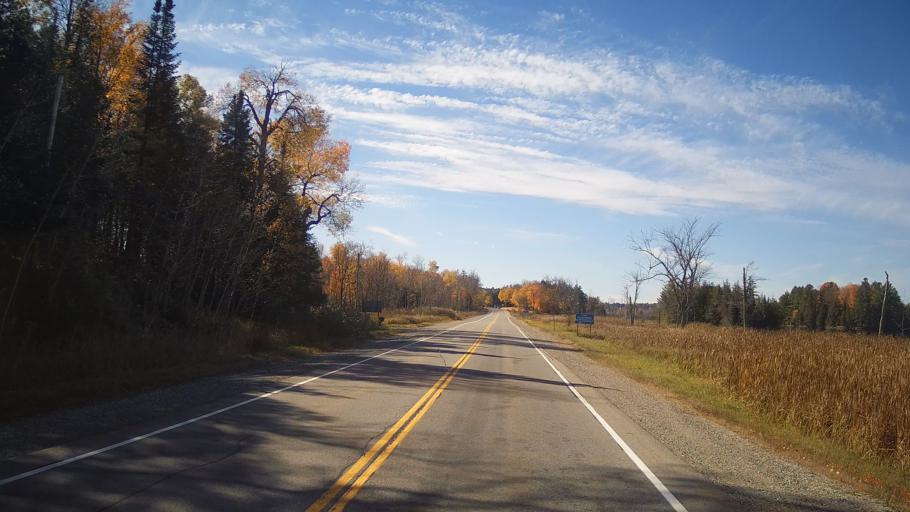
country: CA
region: Ontario
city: Perth
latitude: 44.8266
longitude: -76.5910
